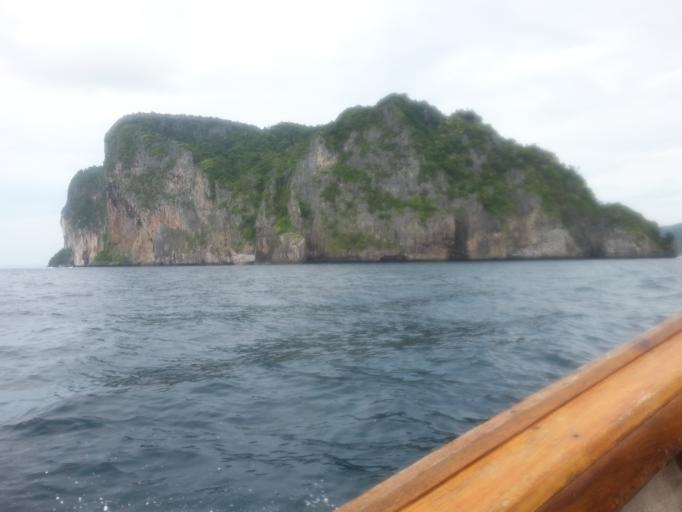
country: TH
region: Krabi
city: Saladan
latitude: 7.7131
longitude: 98.7689
